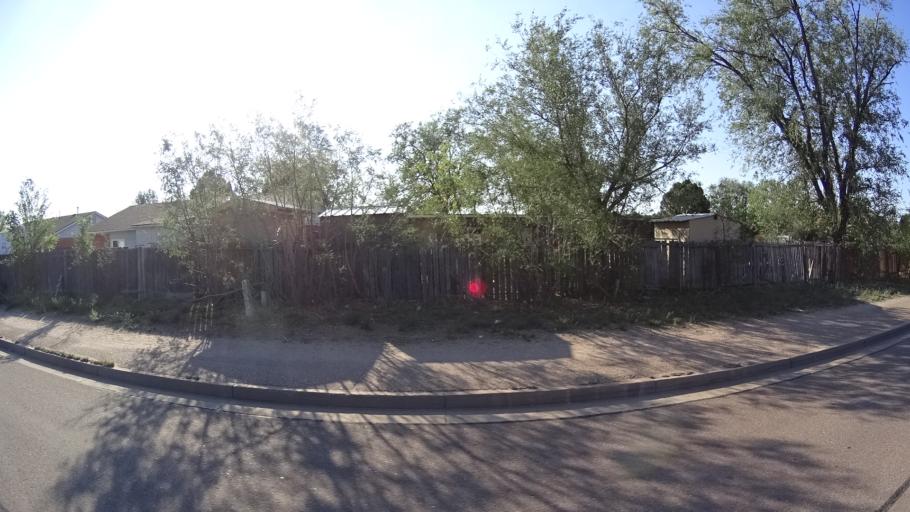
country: US
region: Colorado
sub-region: El Paso County
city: Stratmoor
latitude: 38.7720
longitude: -104.7966
